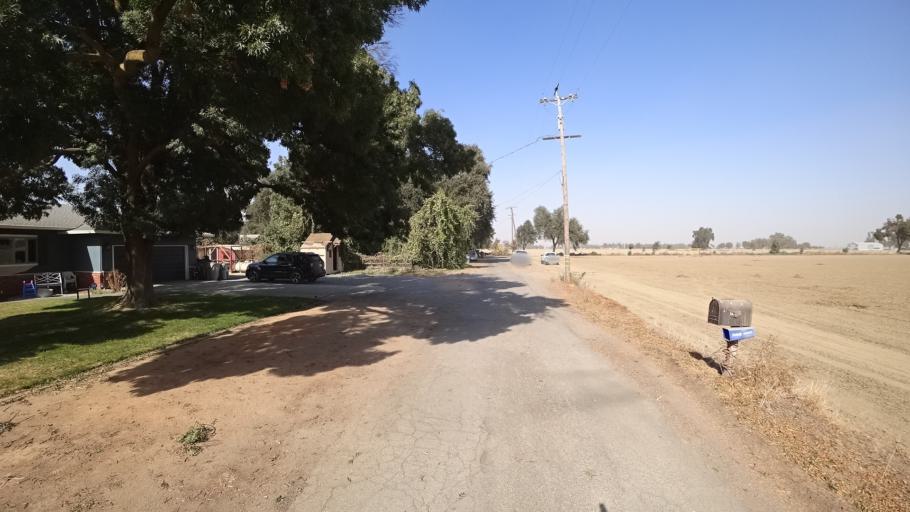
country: US
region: California
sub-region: Yolo County
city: Woodland
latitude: 38.7344
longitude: -121.7813
